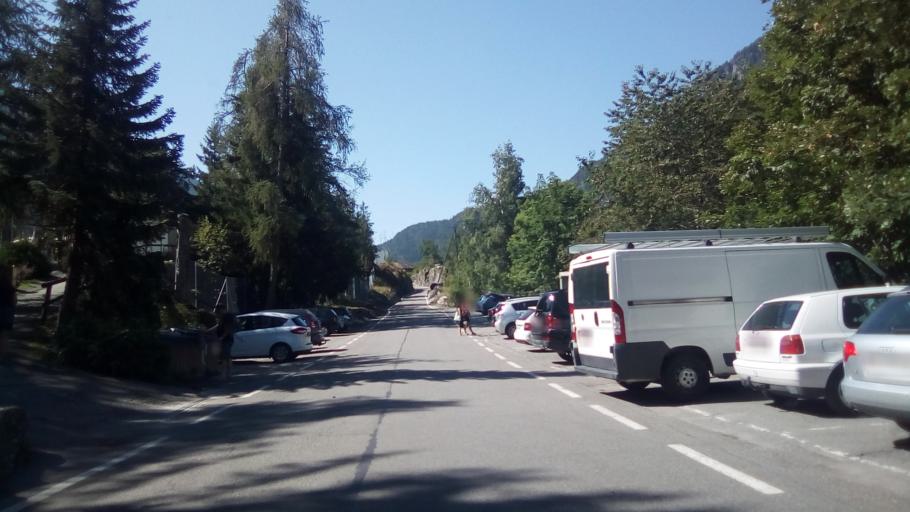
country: CH
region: Valais
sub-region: Saint-Maurice District
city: Salvan
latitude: 46.1103
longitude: 7.0098
